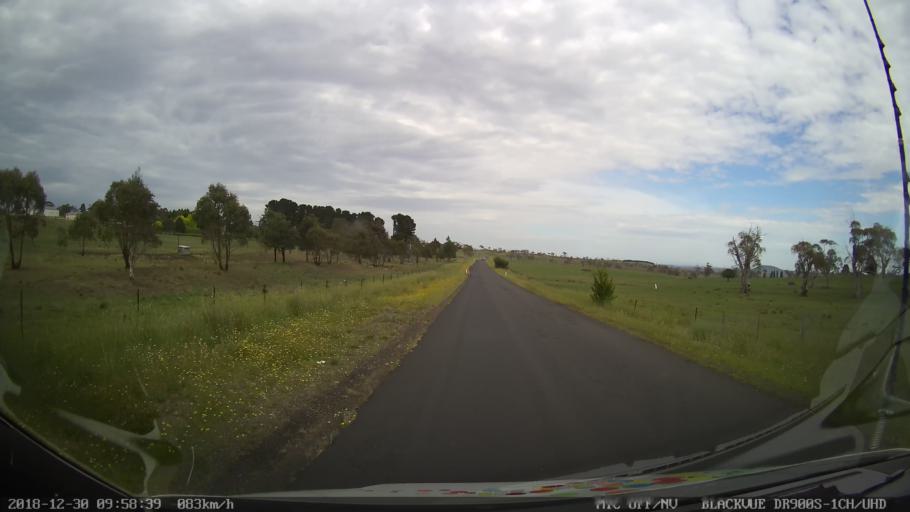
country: AU
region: New South Wales
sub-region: Cooma-Monaro
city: Cooma
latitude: -36.5222
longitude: 149.2229
